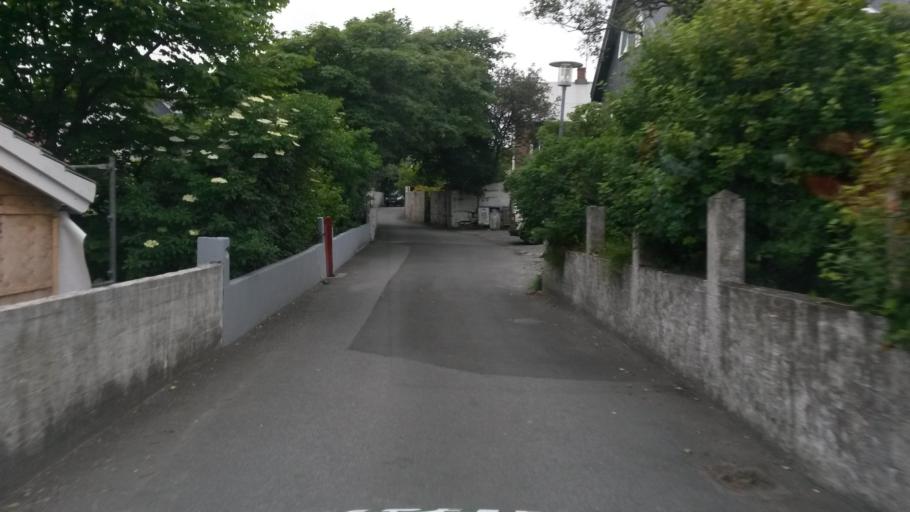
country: FO
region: Streymoy
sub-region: Torshavn
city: Torshavn
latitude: 62.0125
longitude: -6.7731
